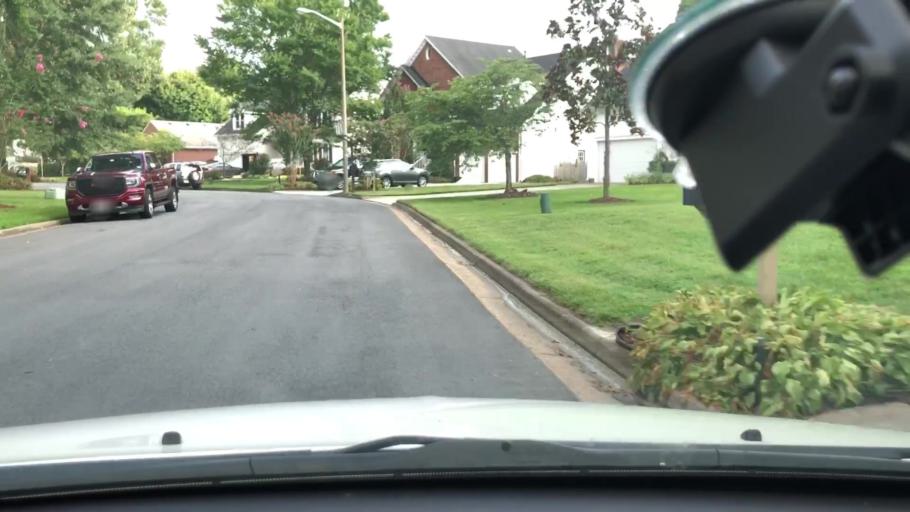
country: US
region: Virginia
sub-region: City of Chesapeake
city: Chesapeake
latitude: 36.7155
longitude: -76.2722
